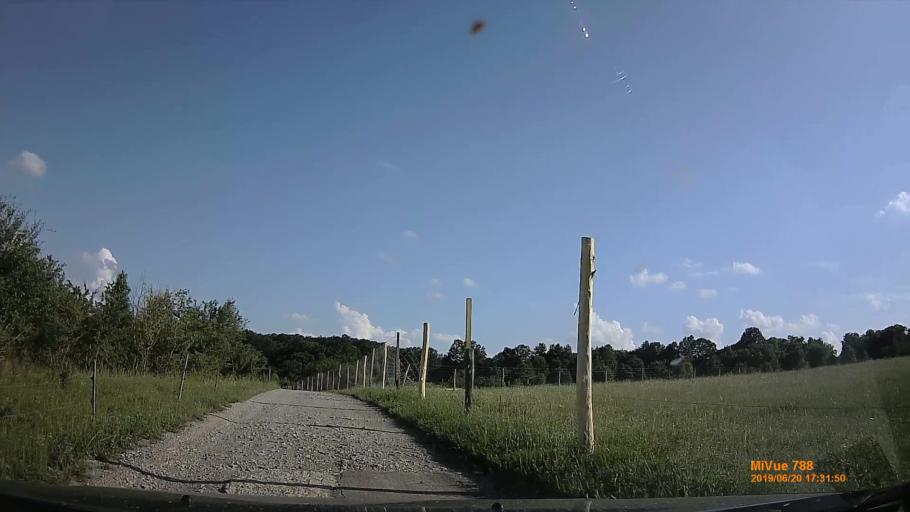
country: HU
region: Baranya
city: Buekkoesd
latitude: 46.1511
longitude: 18.0096
